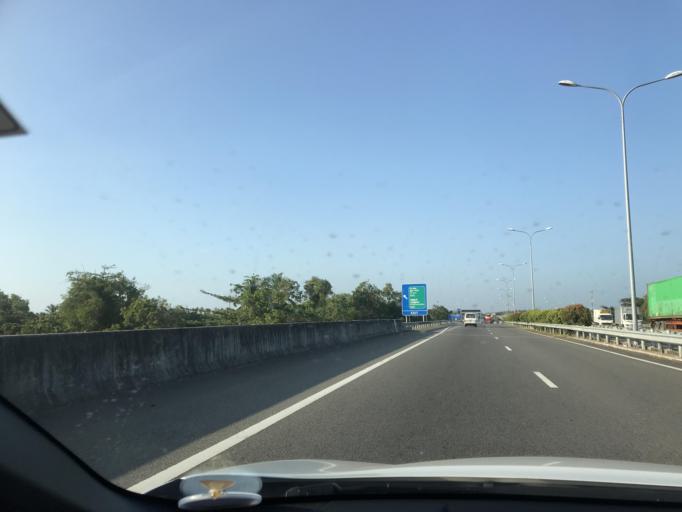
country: LK
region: Western
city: Ja Ela
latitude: 7.0765
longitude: 79.8776
